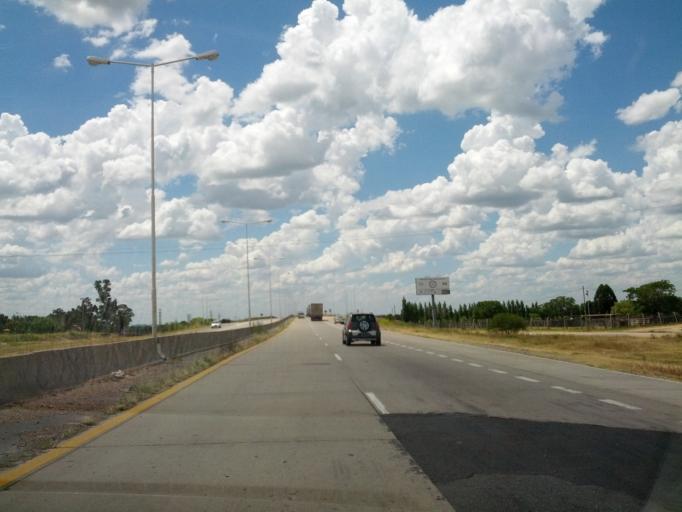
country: AR
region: Entre Rios
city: Gualeguaychu
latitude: -33.0159
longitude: -58.6085
